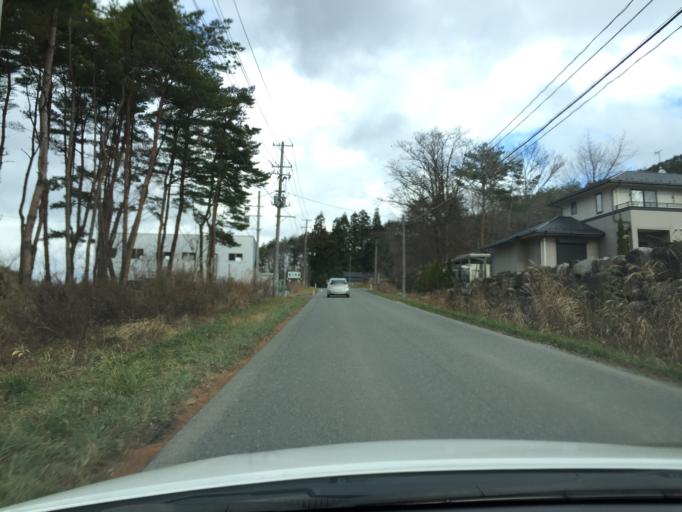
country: JP
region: Fukushima
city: Yanagawamachi-saiwaicho
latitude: 37.6977
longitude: 140.6975
